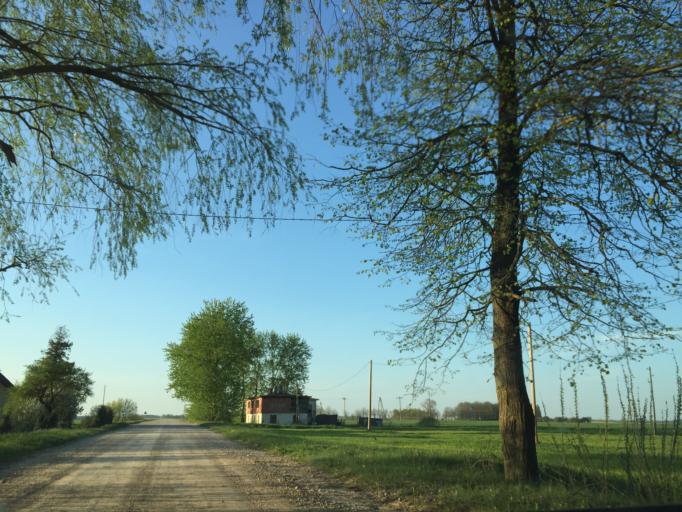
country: LV
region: Bauskas Rajons
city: Bauska
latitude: 56.2764
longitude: 24.1952
